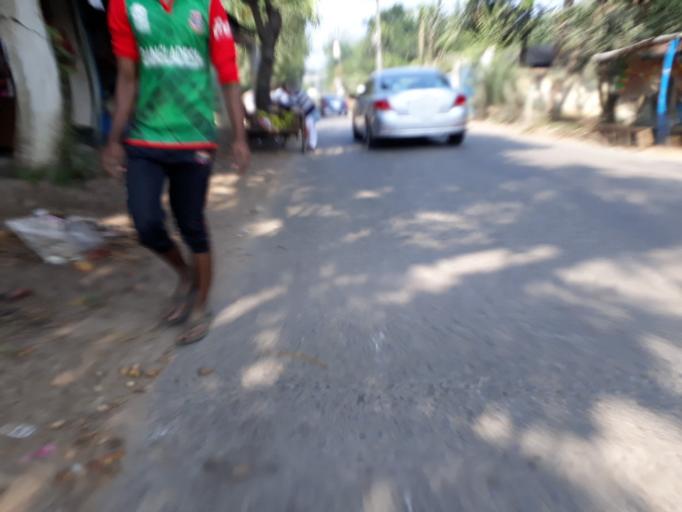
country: BD
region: Dhaka
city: Tungi
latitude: 23.8685
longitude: 90.3101
